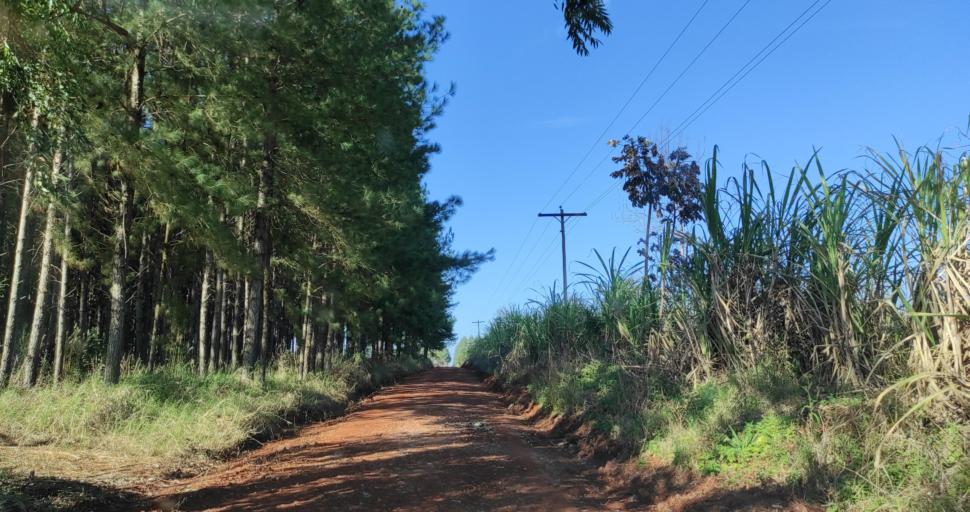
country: AR
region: Misiones
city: Capiovi
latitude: -26.8812
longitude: -55.0371
